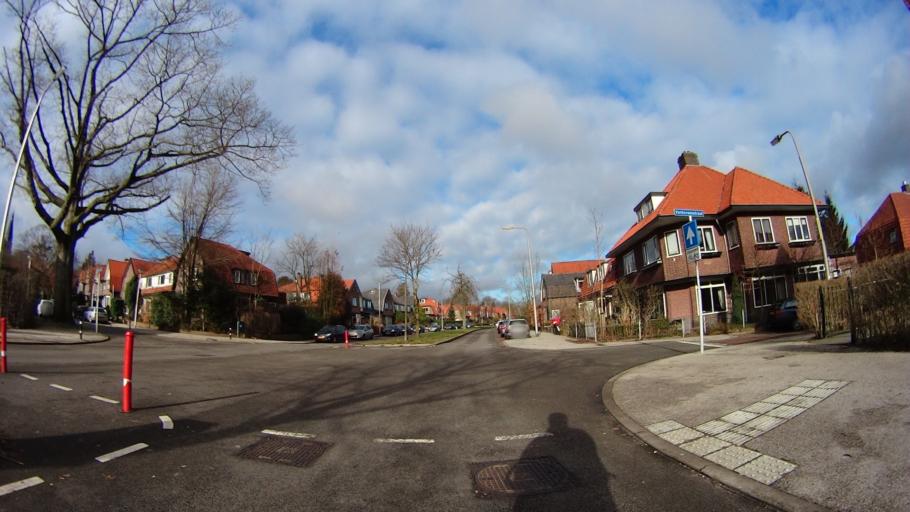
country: NL
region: Utrecht
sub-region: Gemeente Amersfoort
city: Amersfoort
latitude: 52.1436
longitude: 5.3760
